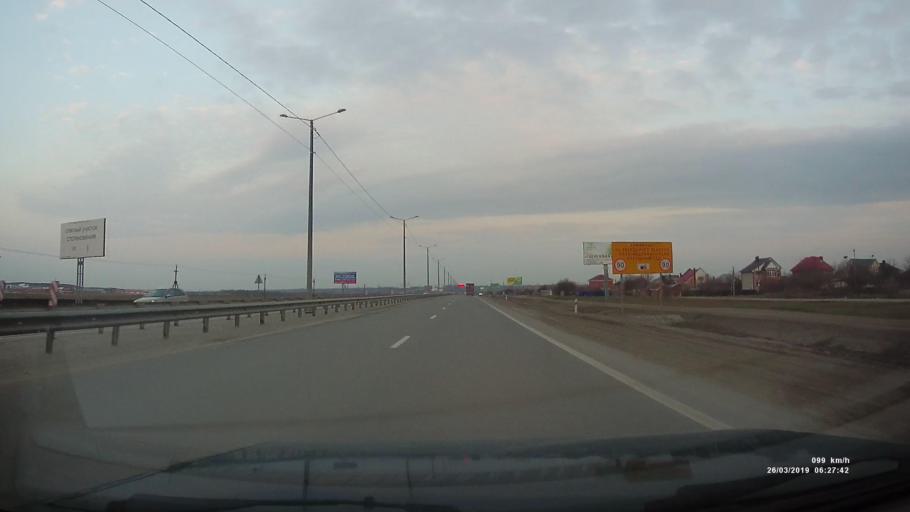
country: RU
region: Rostov
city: Kalinin
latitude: 47.2620
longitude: 39.6084
